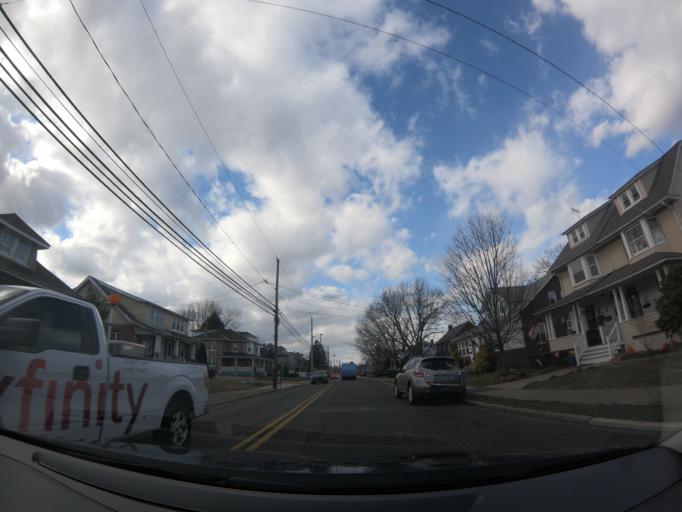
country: US
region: Pennsylvania
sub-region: Montgomery County
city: Telford
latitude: 40.3232
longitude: -75.3249
